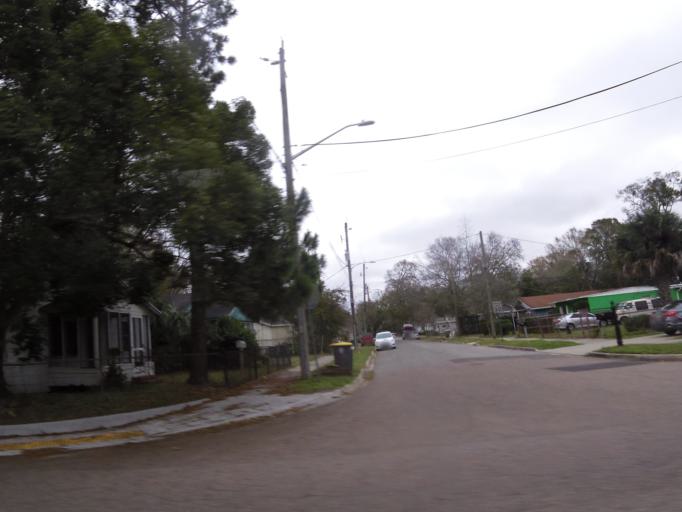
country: US
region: Florida
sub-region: Duval County
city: Jacksonville
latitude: 30.3580
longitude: -81.6865
